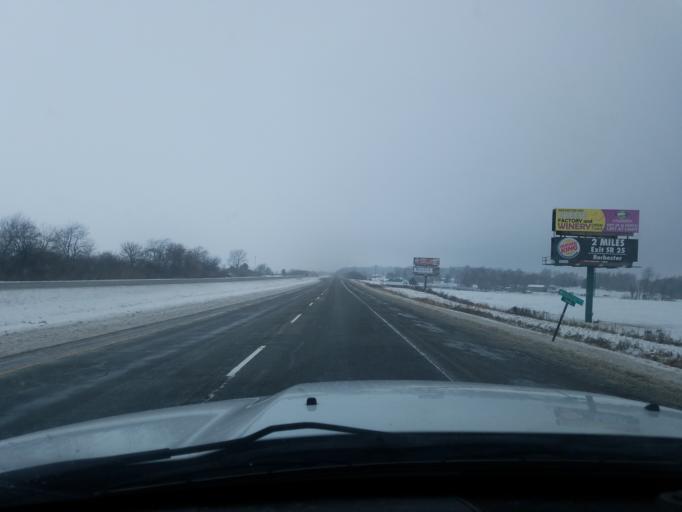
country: US
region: Indiana
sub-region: Fulton County
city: Rochester
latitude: 41.0314
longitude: -86.1847
